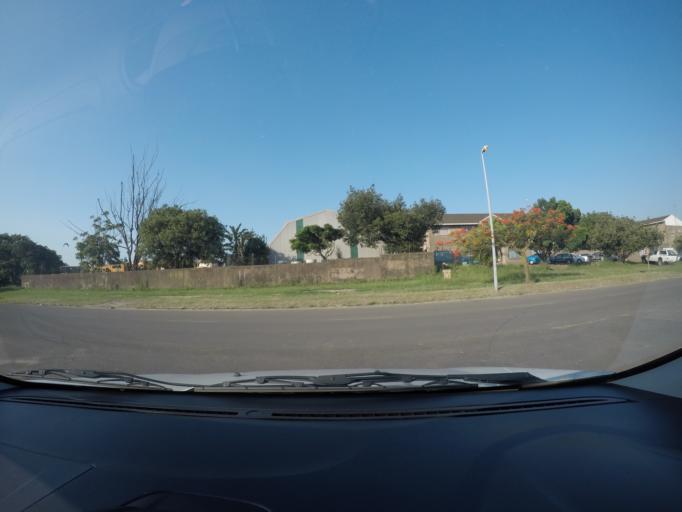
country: ZA
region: KwaZulu-Natal
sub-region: uThungulu District Municipality
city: Richards Bay
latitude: -28.7506
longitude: 32.0168
